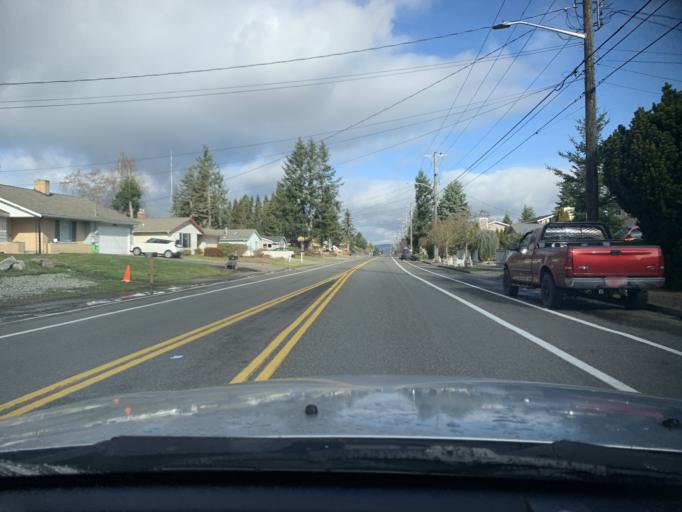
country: US
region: Washington
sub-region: Pierce County
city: Fircrest
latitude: 47.2831
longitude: -122.5211
